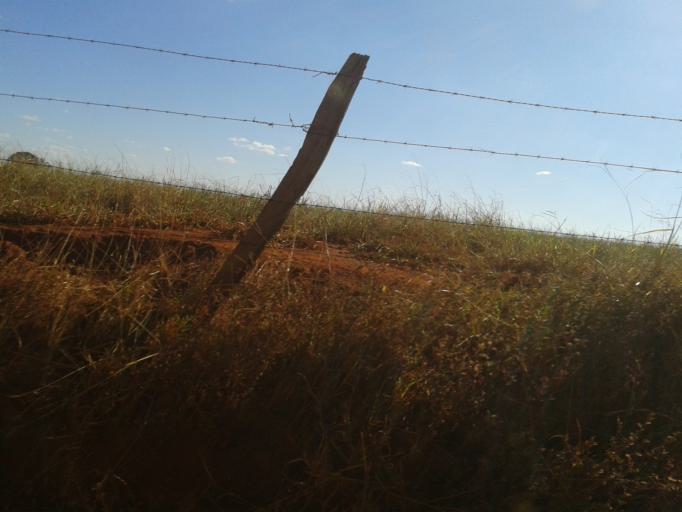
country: BR
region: Minas Gerais
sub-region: Centralina
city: Centralina
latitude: -18.7498
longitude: -49.1878
